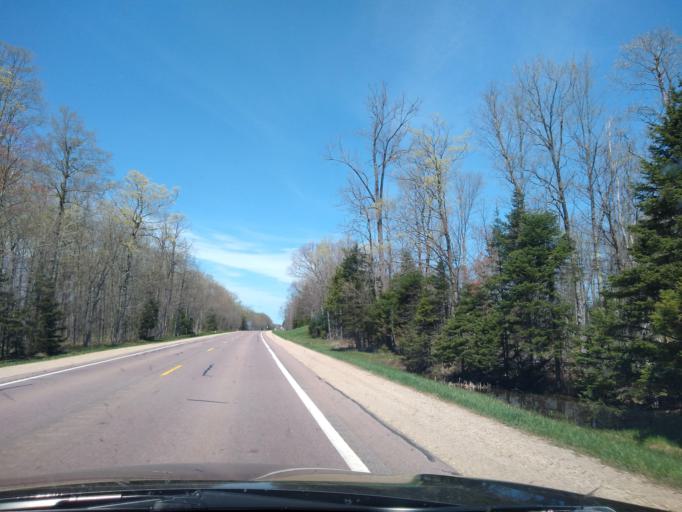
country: US
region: Michigan
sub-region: Marquette County
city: K. I. Sawyer Air Force Base
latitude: 46.2370
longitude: -87.0739
